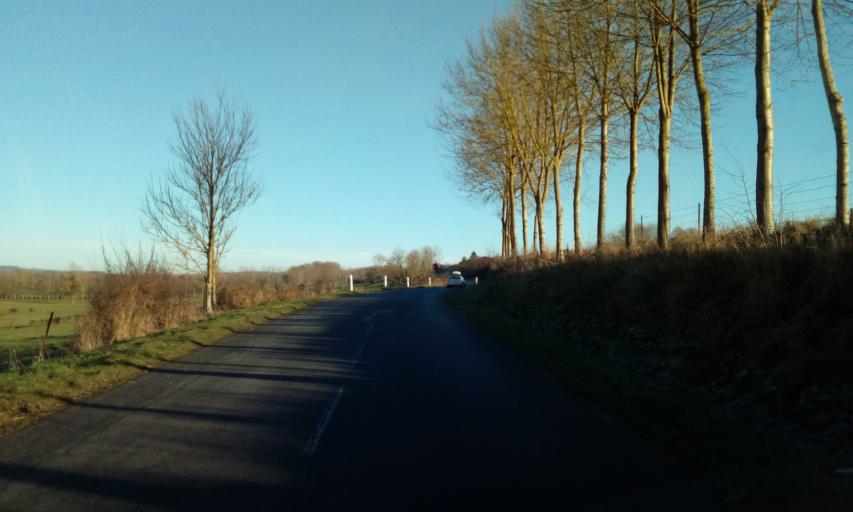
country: FR
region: Picardie
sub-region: Departement de l'Aisne
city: Rozoy-sur-Serre
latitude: 49.7078
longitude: 4.1432
